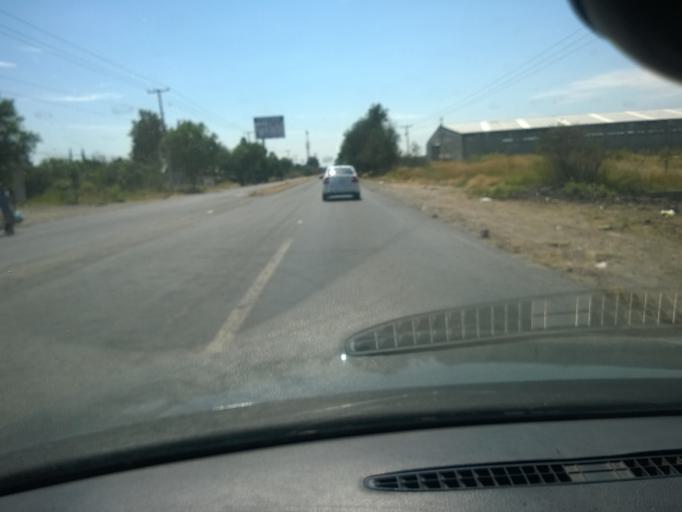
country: MX
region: Guanajuato
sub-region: Leon
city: El CERESO
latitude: 20.9857
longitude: -101.7021
